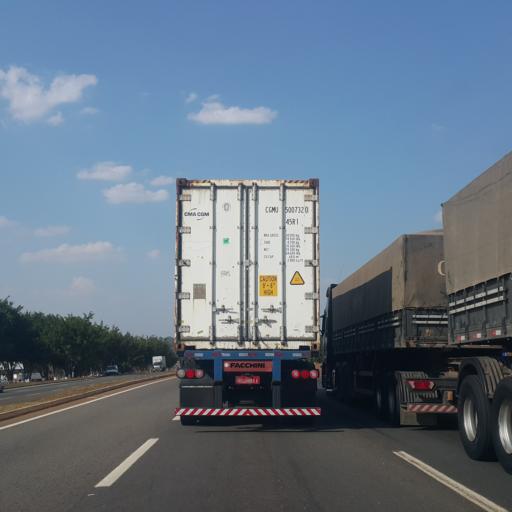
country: BR
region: Goias
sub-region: Anapolis
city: Anapolis
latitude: -16.3007
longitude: -48.8128
